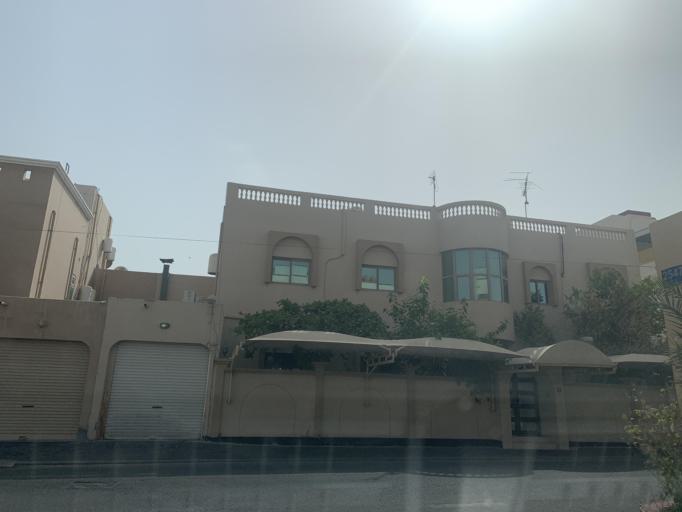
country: BH
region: Northern
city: Ar Rifa'
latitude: 26.1274
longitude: 50.5694
